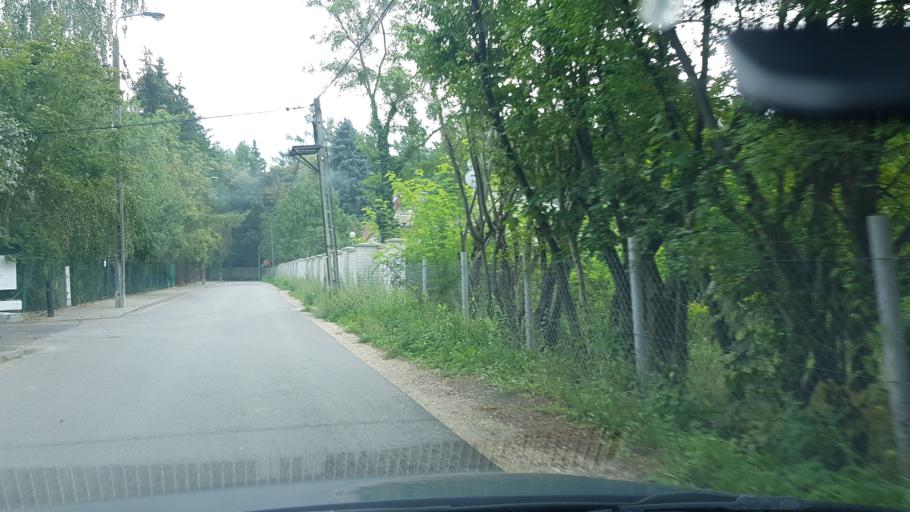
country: PL
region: Masovian Voivodeship
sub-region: Powiat piaseczynski
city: Konstancin-Jeziorna
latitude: 52.1020
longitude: 21.1076
